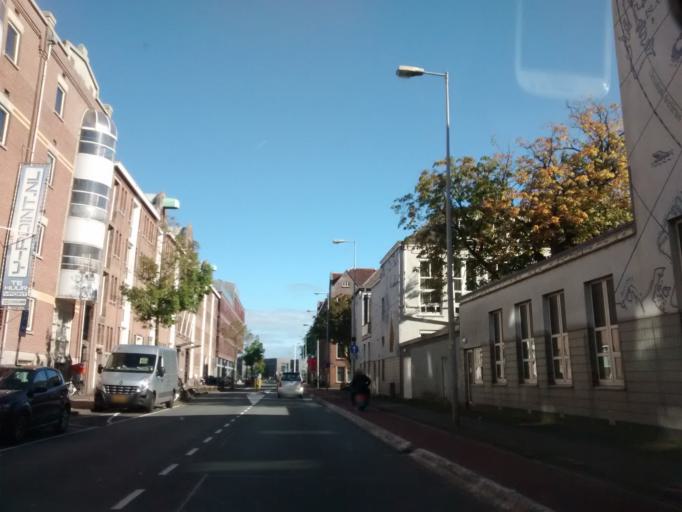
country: NL
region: North Holland
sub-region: Gemeente Amsterdam
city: Amsterdam
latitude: 52.3901
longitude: 4.8879
